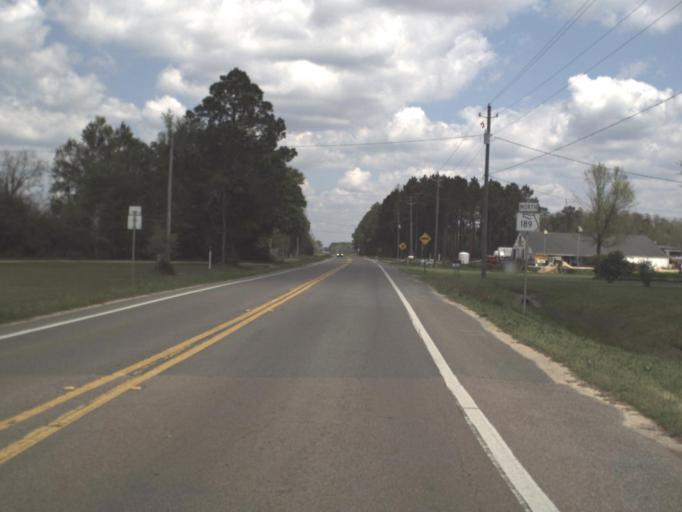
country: US
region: Florida
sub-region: Okaloosa County
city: Crestview
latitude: 30.7986
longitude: -86.6812
